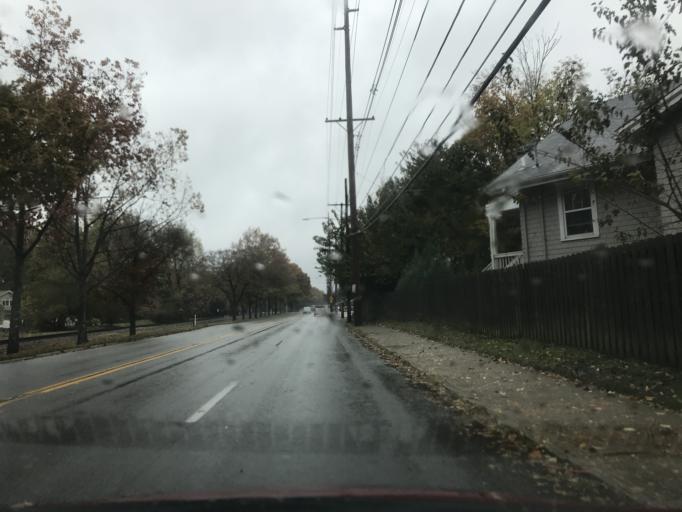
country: US
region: Kentucky
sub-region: Jefferson County
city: Saint Matthews
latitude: 38.2544
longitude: -85.6778
